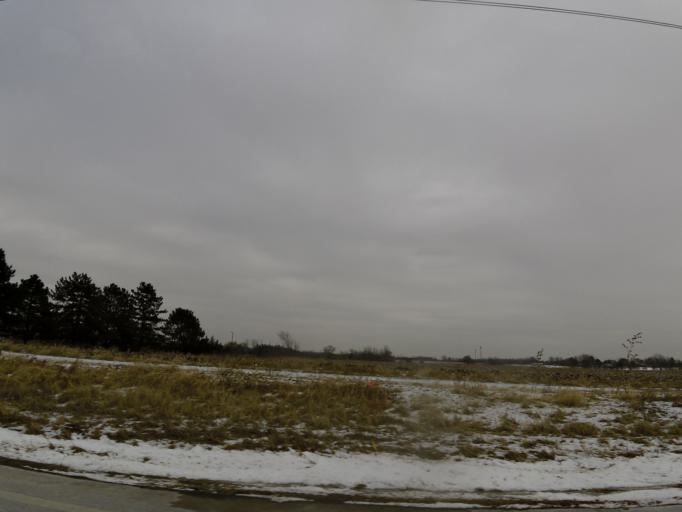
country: US
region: Minnesota
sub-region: Hennepin County
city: Medina
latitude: 45.0476
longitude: -93.5633
